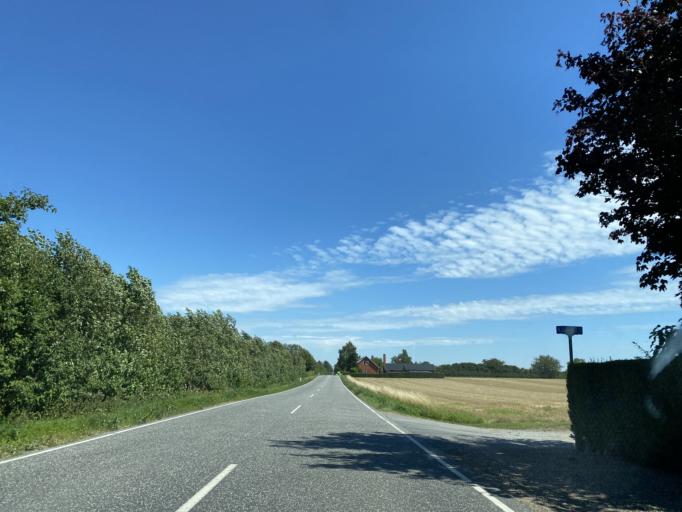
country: DK
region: South Denmark
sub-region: Nyborg Kommune
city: Ullerslev
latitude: 55.2538
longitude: 10.6528
